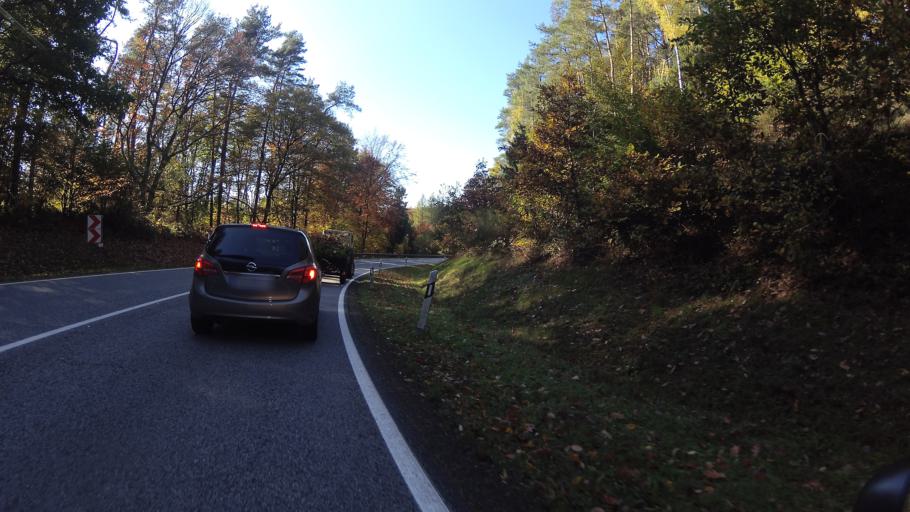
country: DE
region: Saarland
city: Losheim
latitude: 49.4950
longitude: 6.7267
